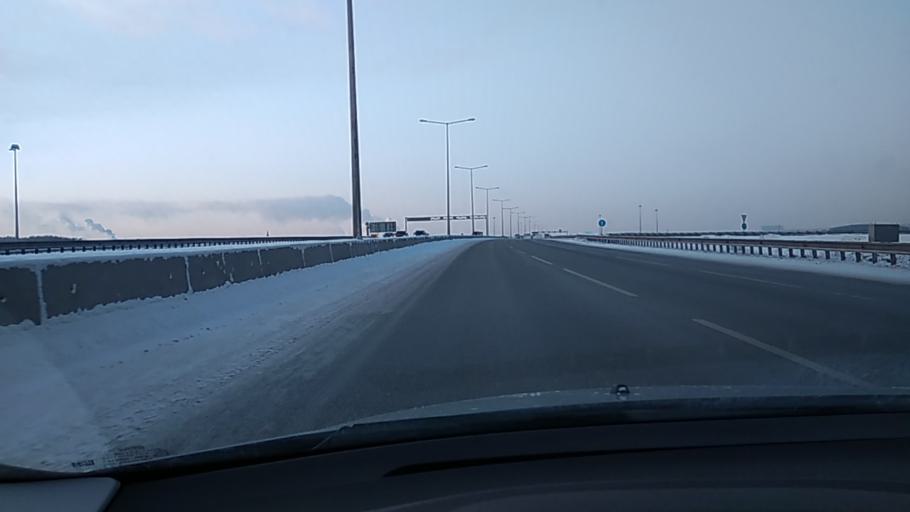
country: RU
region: Sverdlovsk
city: Istok
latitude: 56.7613
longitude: 60.7756
